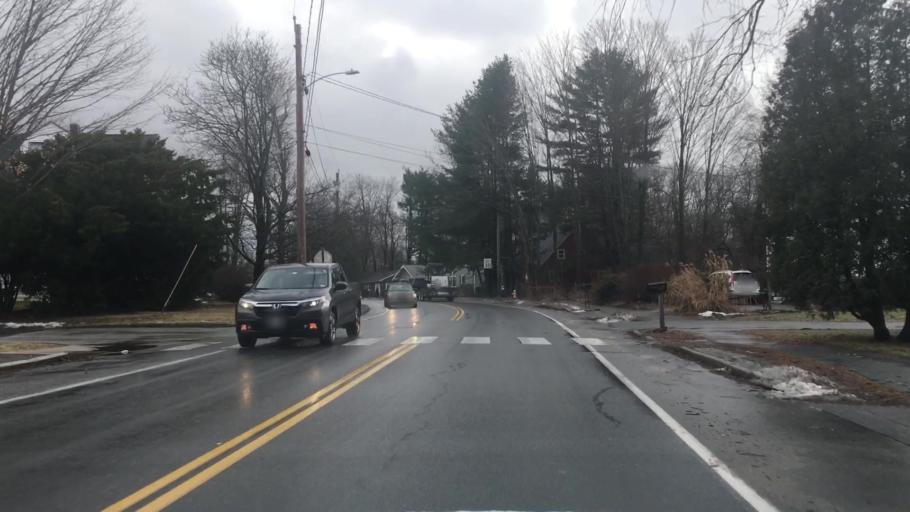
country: US
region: Maine
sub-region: Cumberland County
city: South Portland Gardens
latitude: 43.6715
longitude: -70.3138
